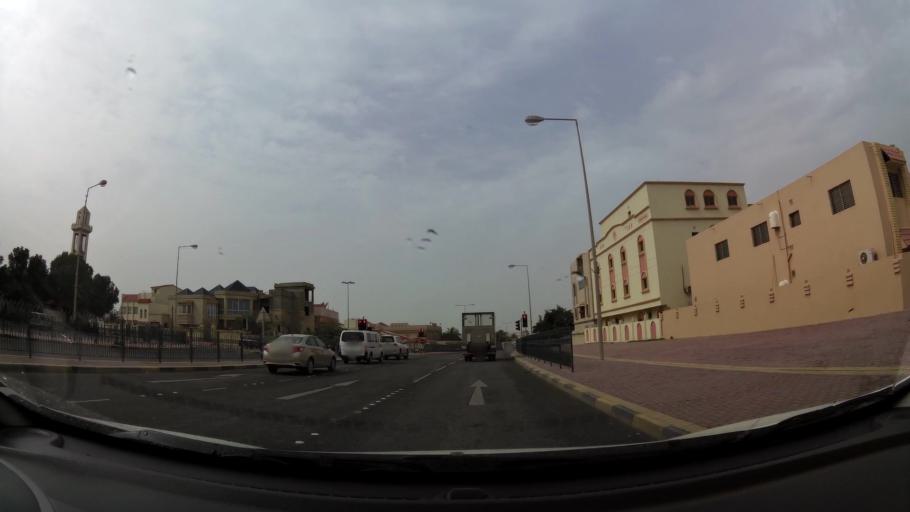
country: BH
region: Northern
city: Ar Rifa'
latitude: 26.1387
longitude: 50.5589
